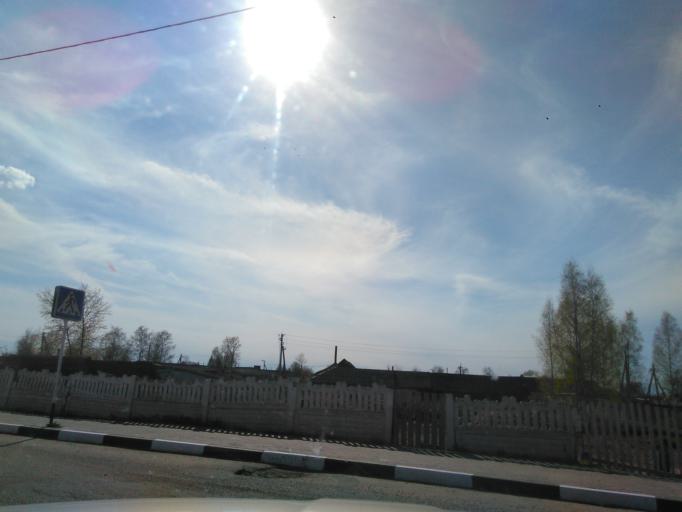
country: BY
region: Vitebsk
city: Chashniki
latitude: 54.8601
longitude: 29.1607
